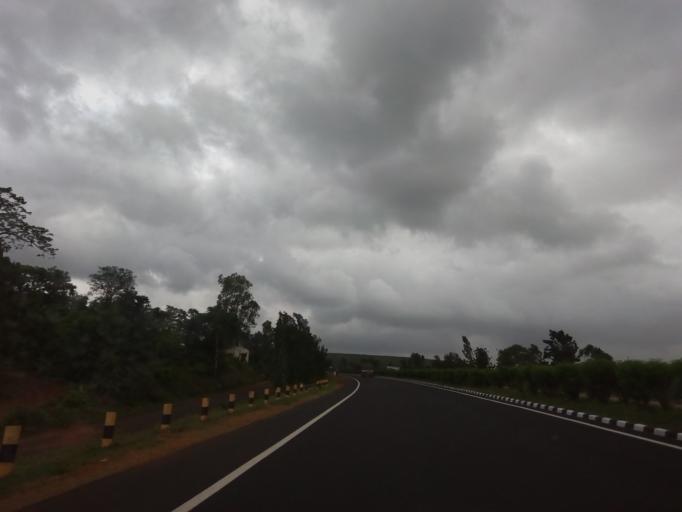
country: IN
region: Karnataka
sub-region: Belgaum
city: Hukeri
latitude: 16.0637
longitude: 74.5155
